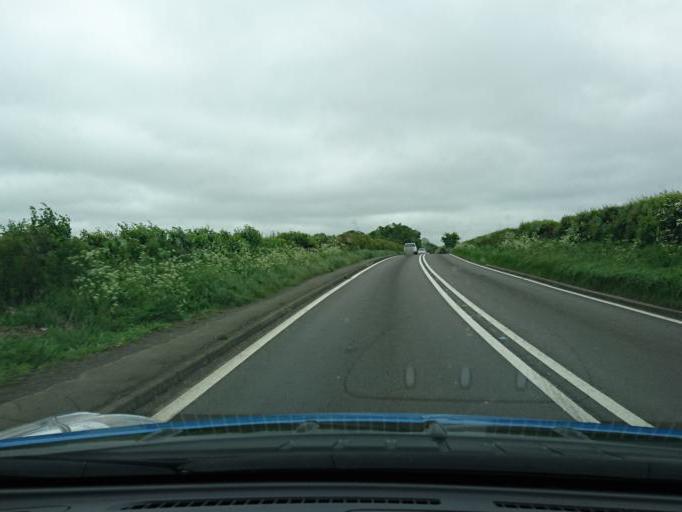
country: GB
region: England
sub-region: Oxfordshire
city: Faringdon
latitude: 51.6709
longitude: -1.5429
